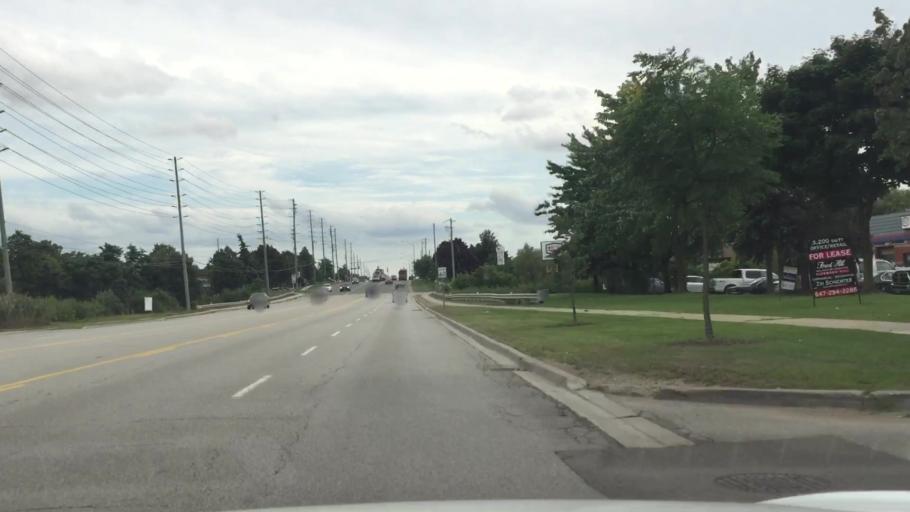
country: CA
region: Ontario
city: Vaughan
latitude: 43.8220
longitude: -79.5049
